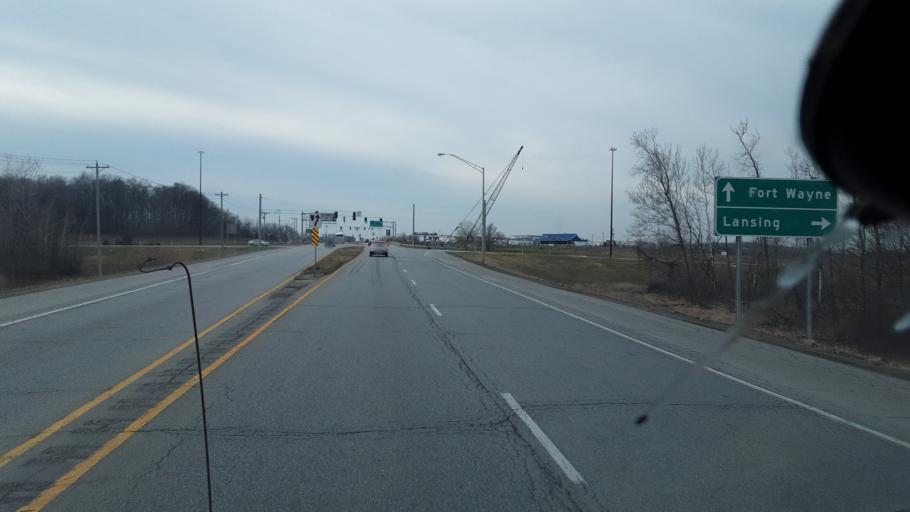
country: US
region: Indiana
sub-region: DeKalb County
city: Waterloo
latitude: 41.4398
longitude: -85.0505
